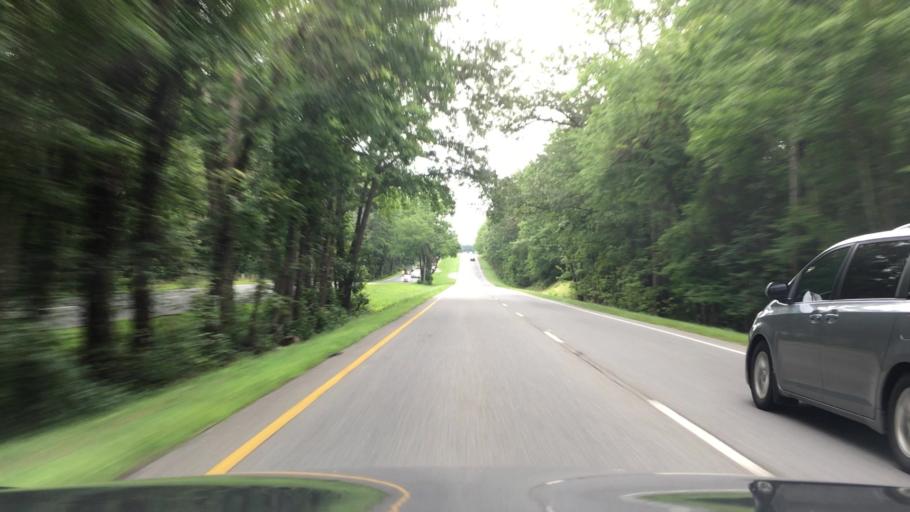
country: US
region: Virginia
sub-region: Spotsylvania County
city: Spotsylvania
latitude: 38.3100
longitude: -77.6464
